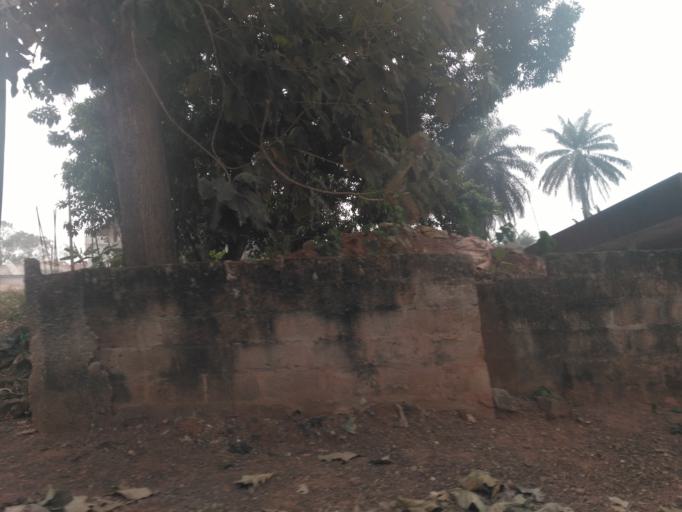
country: GH
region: Ashanti
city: Kumasi
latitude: 6.6789
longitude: -1.6194
